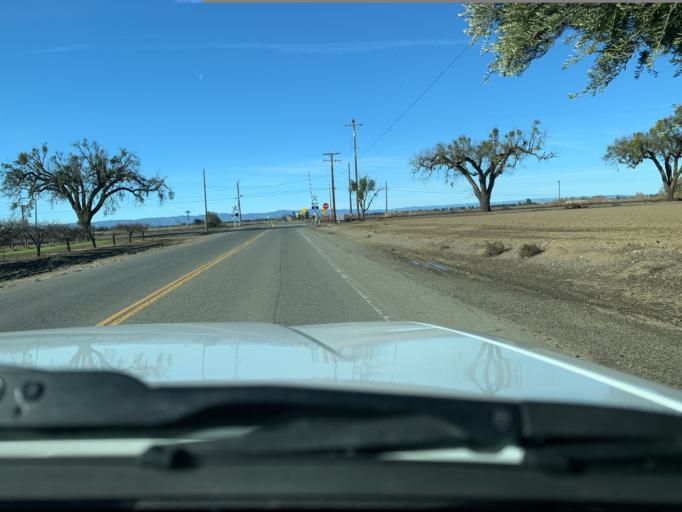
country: US
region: California
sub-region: Yolo County
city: Woodland
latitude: 38.6411
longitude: -121.7650
